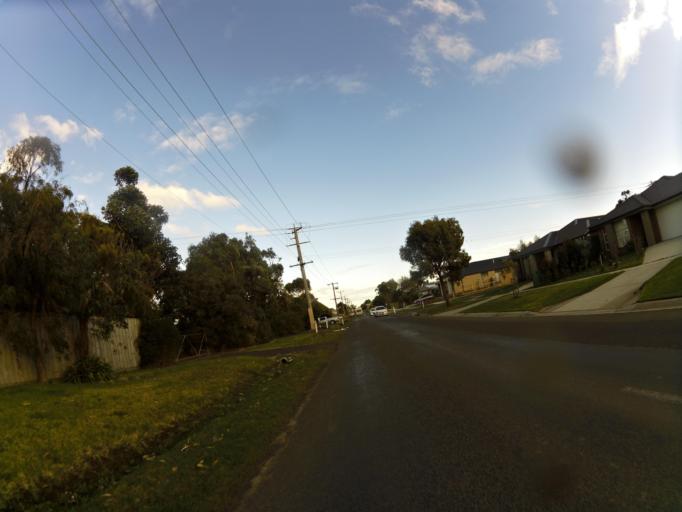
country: AU
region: Victoria
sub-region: Bass Coast
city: North Wonthaggi
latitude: -38.5603
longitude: 145.5480
